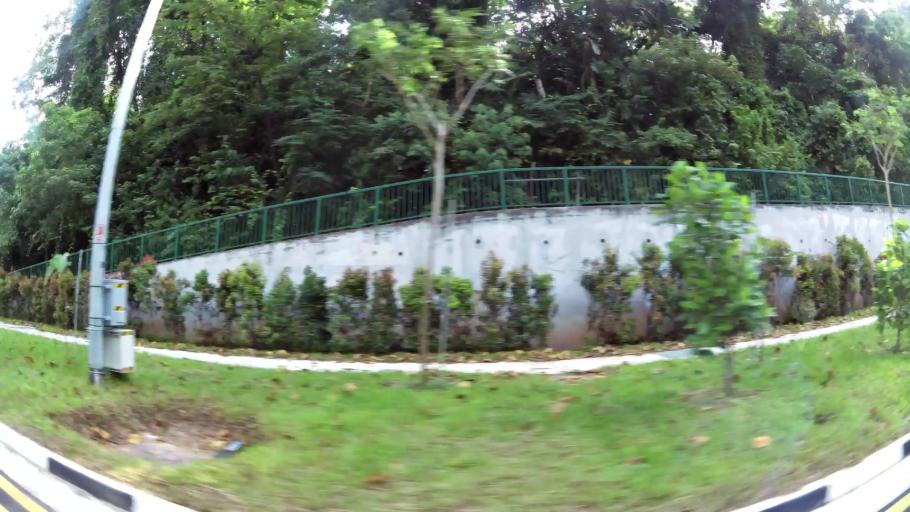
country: SG
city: Singapore
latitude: 1.2697
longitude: 103.8253
